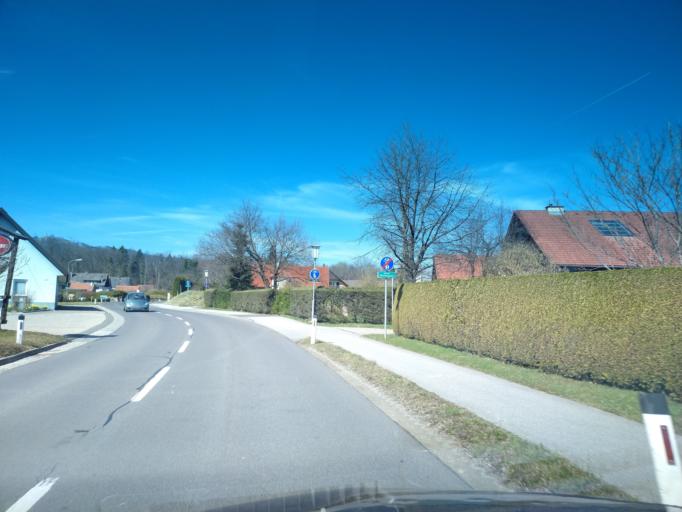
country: AT
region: Styria
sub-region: Politischer Bezirk Deutschlandsberg
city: Hollenegg
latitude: 46.7855
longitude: 15.2398
